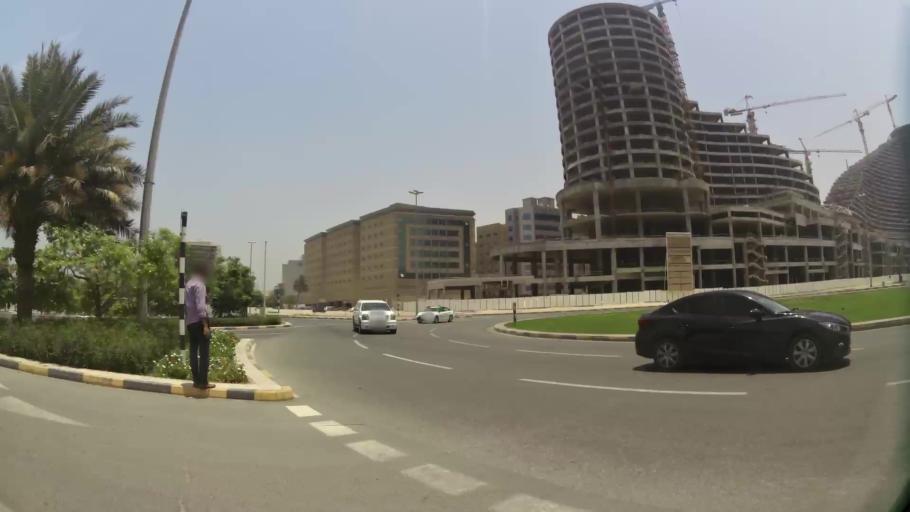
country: AE
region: Ash Shariqah
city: Sharjah
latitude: 25.3312
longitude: 55.3602
